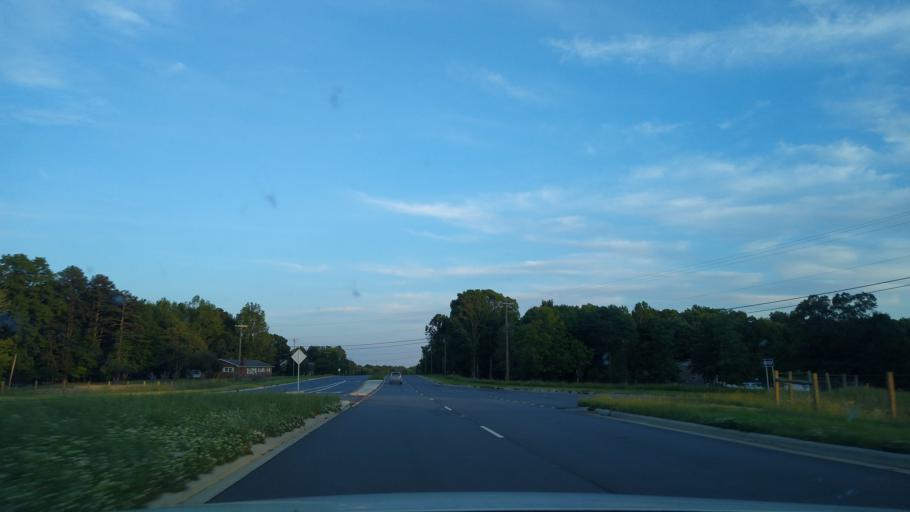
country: US
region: North Carolina
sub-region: Forsyth County
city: Kernersville
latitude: 36.1316
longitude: -80.0508
